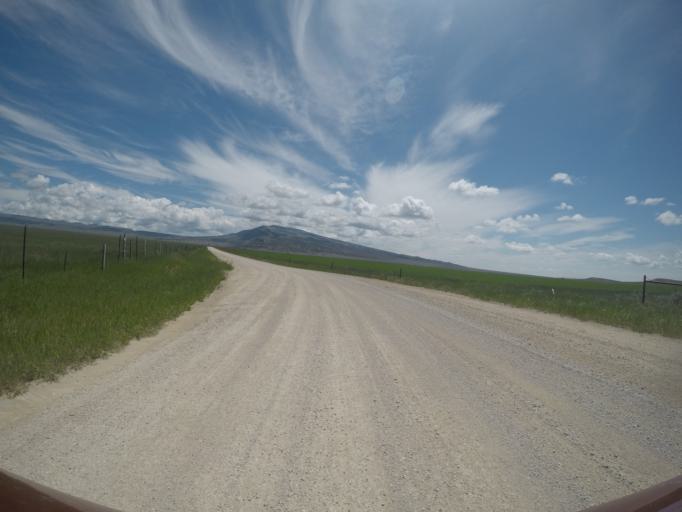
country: US
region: Wyoming
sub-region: Park County
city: Powell
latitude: 45.2051
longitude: -108.7266
